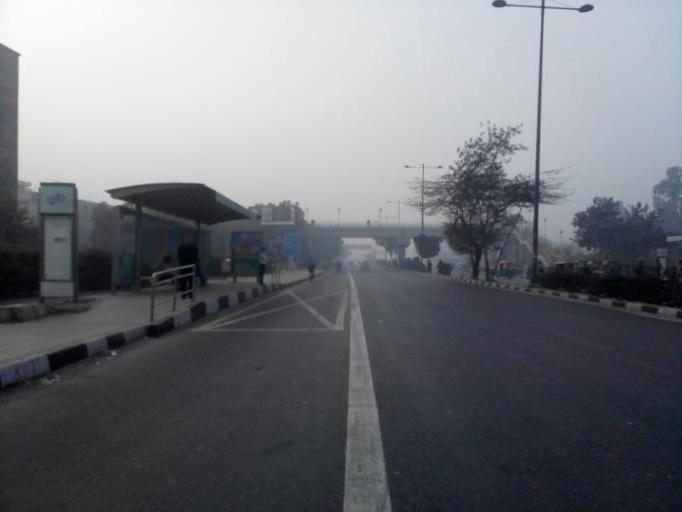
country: IN
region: Uttar Pradesh
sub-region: Gautam Buddha Nagar
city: Noida
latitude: 28.6614
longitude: 77.3203
